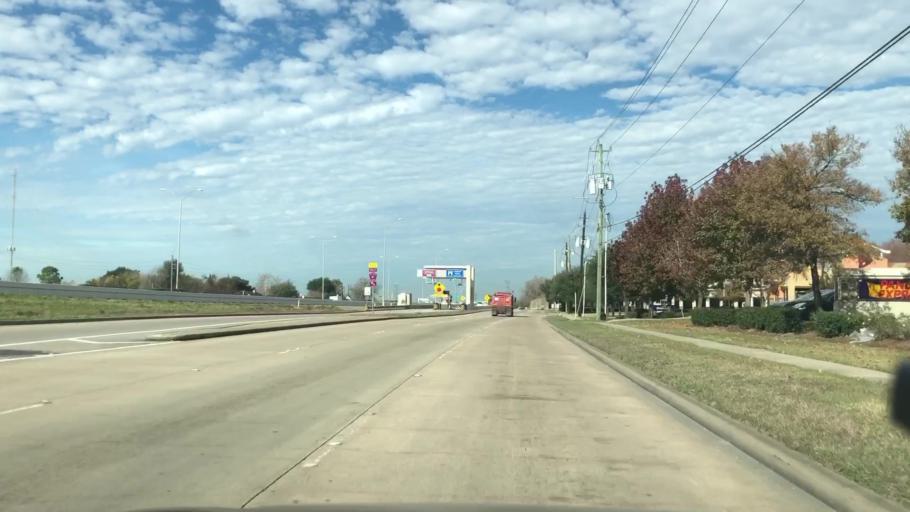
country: US
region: Texas
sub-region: Fort Bend County
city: Missouri City
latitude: 29.6153
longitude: -95.4965
